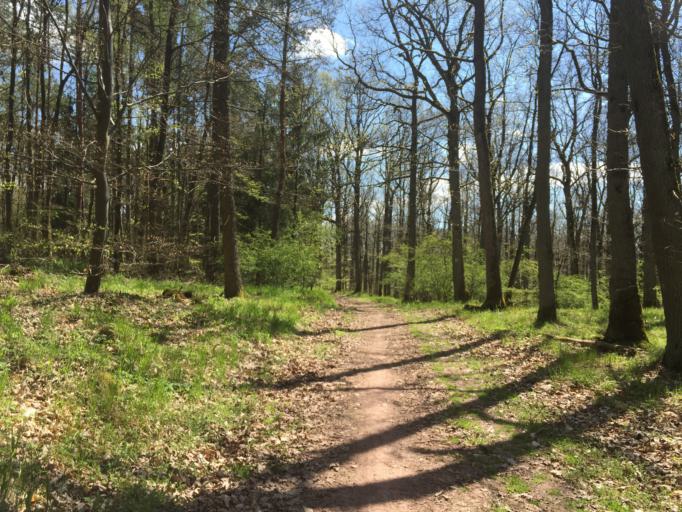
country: DE
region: Bavaria
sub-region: Regierungsbezirk Unterfranken
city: Sulzfeld
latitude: 50.2538
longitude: 10.4531
